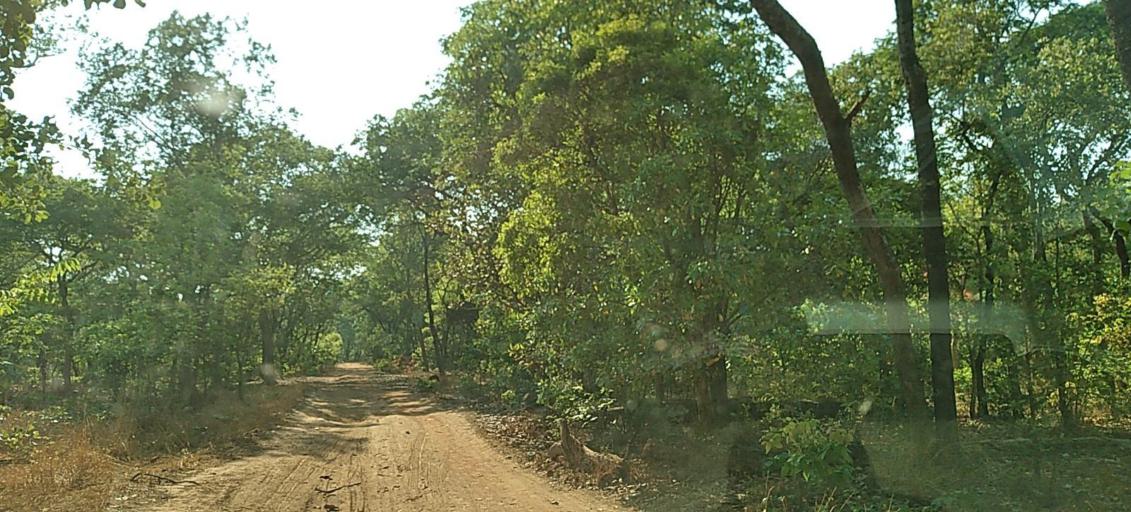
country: ZM
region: Copperbelt
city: Kalulushi
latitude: -13.0063
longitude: 27.7360
